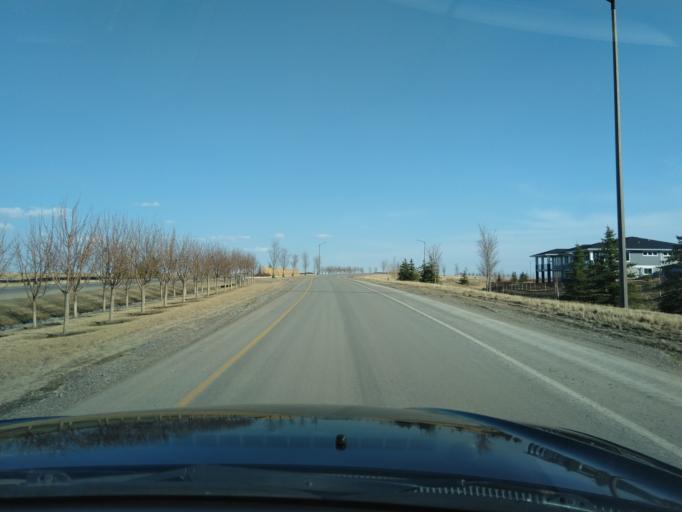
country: CA
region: Alberta
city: Cochrane
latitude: 51.1124
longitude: -114.3923
